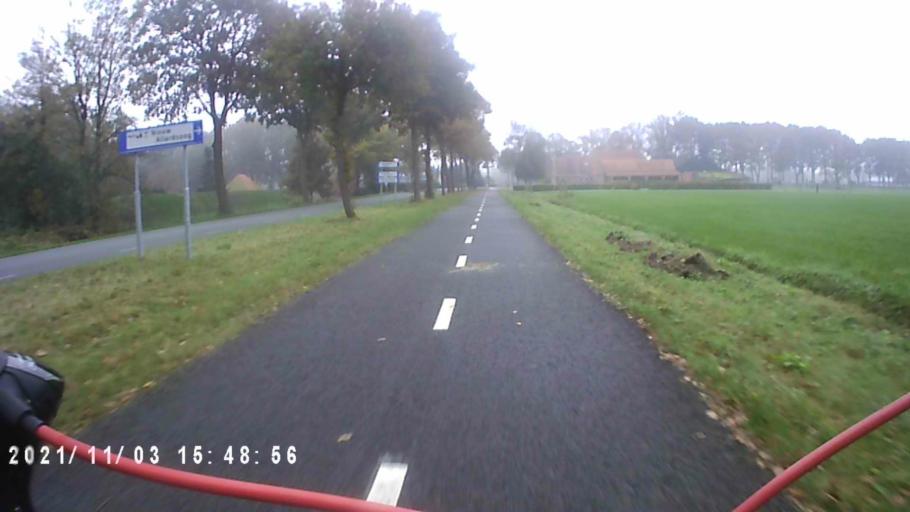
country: NL
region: Groningen
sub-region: Gemeente Leek
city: Leek
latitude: 53.0857
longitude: 6.3386
